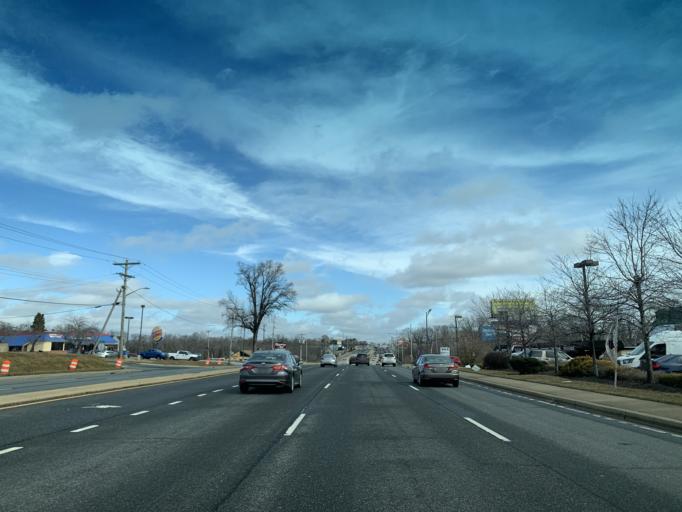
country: US
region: Delaware
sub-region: New Castle County
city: Newport
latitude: 39.7341
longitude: -75.6375
